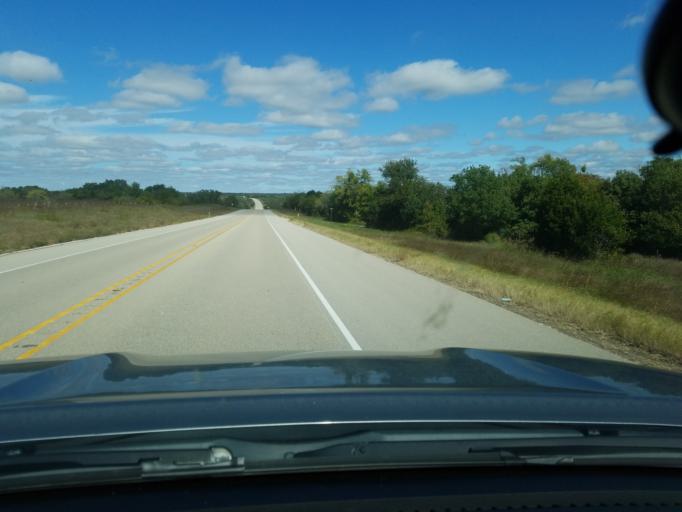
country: US
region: Texas
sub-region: Hamilton County
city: Hamilton
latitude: 31.5756
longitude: -98.1576
